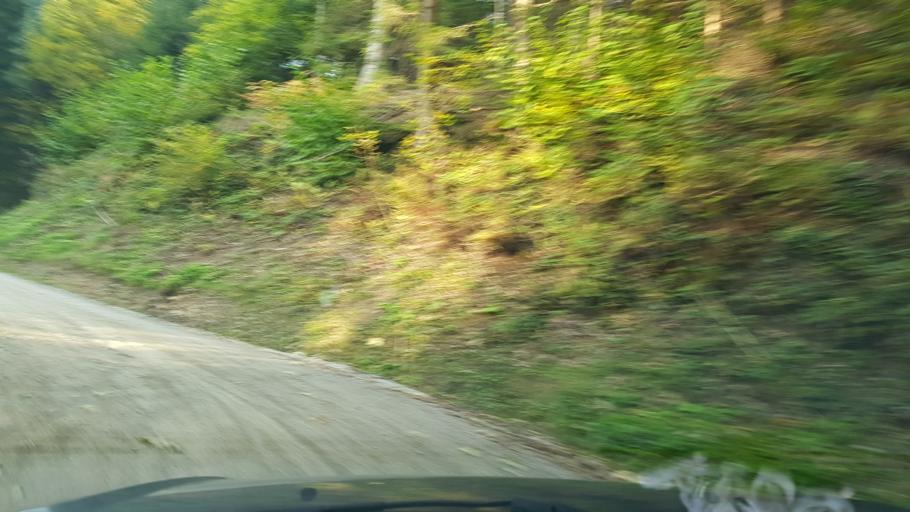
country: SI
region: Slovenj Gradec
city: Legen
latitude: 46.5167
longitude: 15.1289
